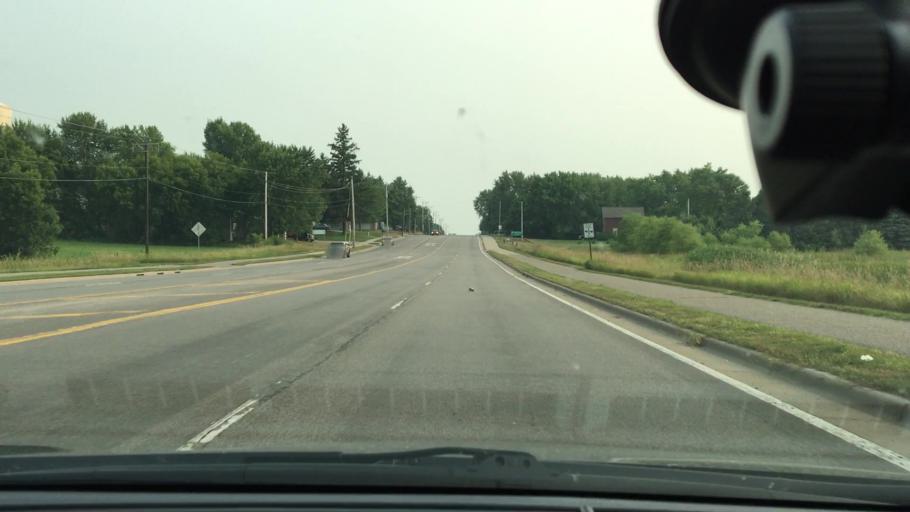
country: US
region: Minnesota
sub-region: Wright County
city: Saint Michael
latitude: 45.2222
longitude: -93.6646
